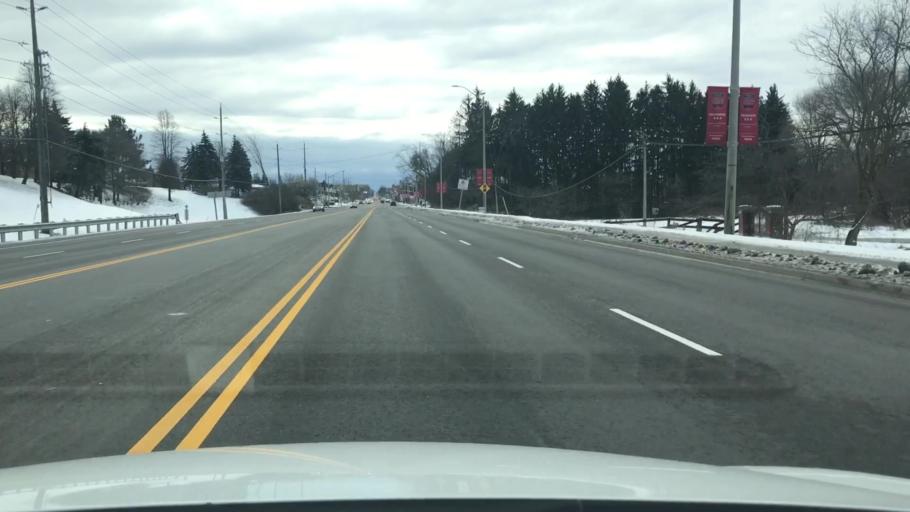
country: CA
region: Ontario
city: Newmarket
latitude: 44.0163
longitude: -79.4716
